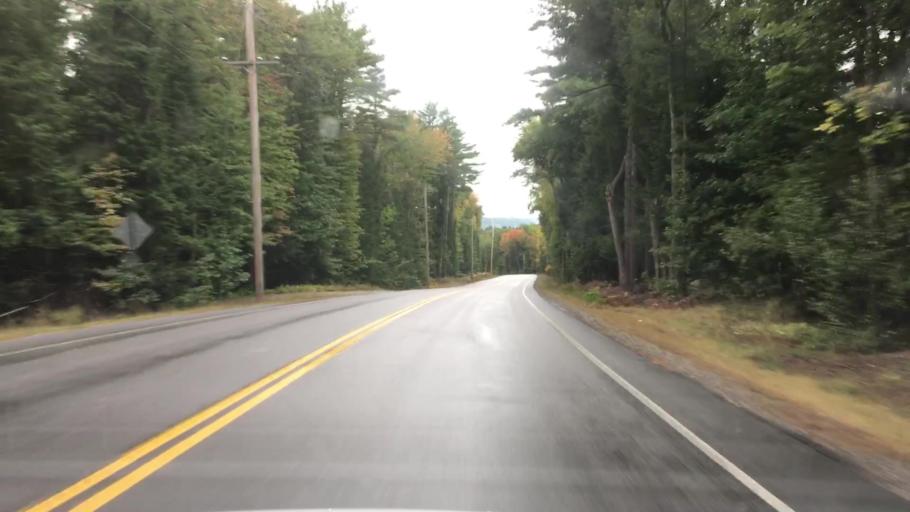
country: US
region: Maine
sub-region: Cumberland County
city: Raymond
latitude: 43.9803
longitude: -70.5333
